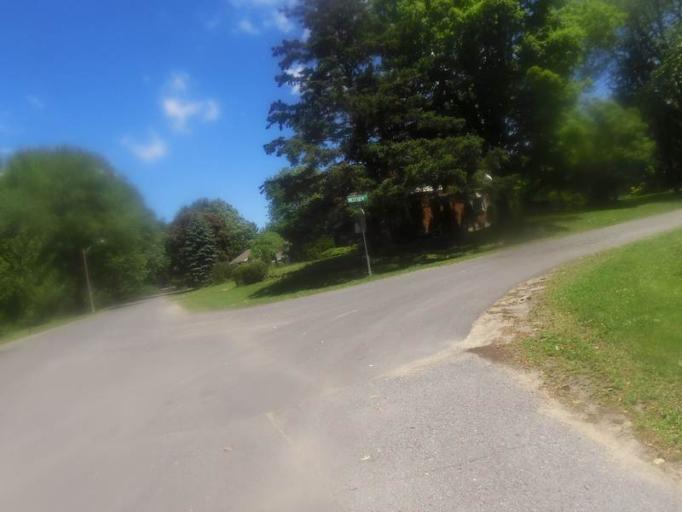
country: CA
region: Ontario
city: Kingston
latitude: 44.2395
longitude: -76.5334
